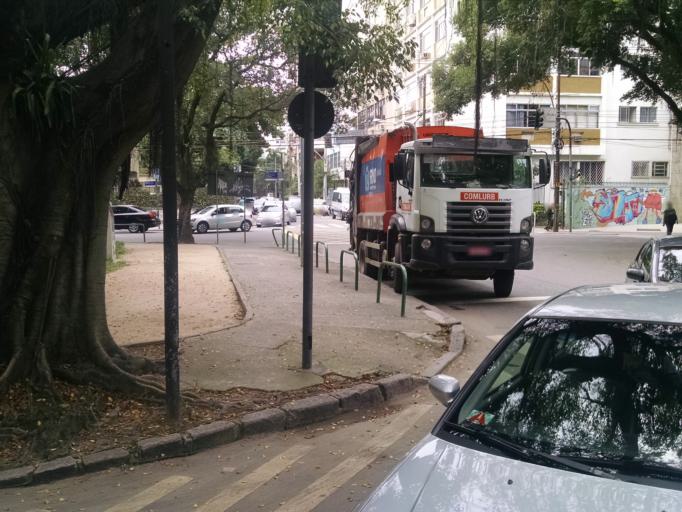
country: BR
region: Rio de Janeiro
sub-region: Rio De Janeiro
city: Rio de Janeiro
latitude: -22.9807
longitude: -43.2240
